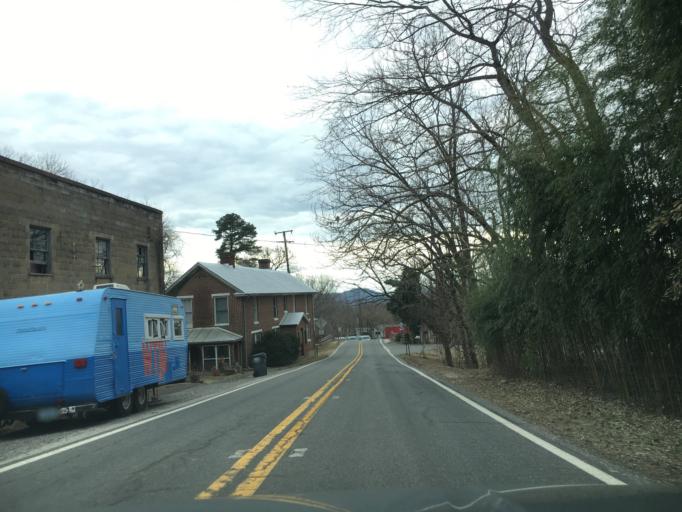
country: US
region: Virginia
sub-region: City of Waynesboro
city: Waynesboro
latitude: 38.0340
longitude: -78.8394
